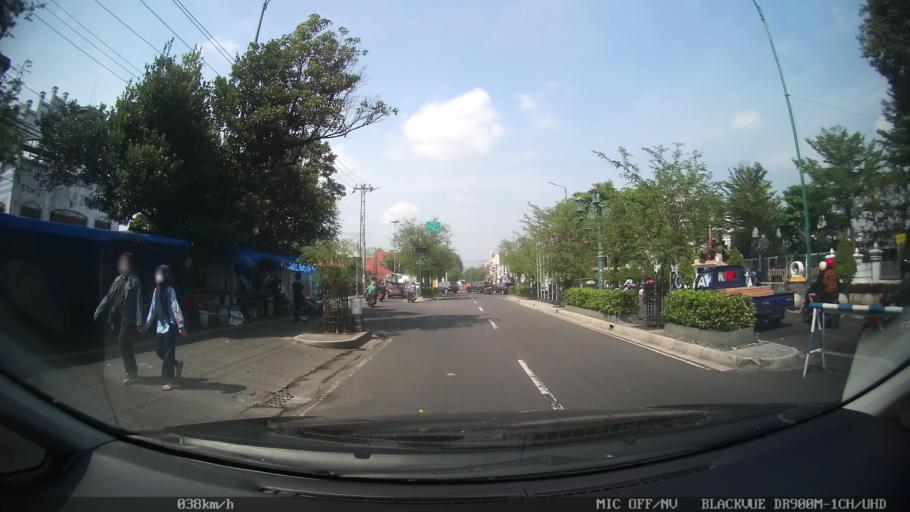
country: ID
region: Daerah Istimewa Yogyakarta
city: Yogyakarta
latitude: -7.7885
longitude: 110.3661
